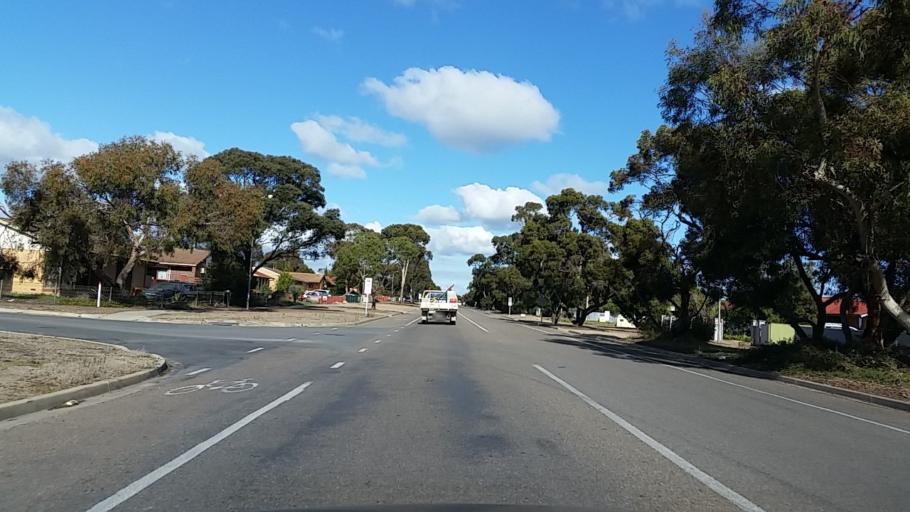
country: AU
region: South Australia
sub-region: Murray Bridge
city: Murray Bridge
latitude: -35.1399
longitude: 139.2854
